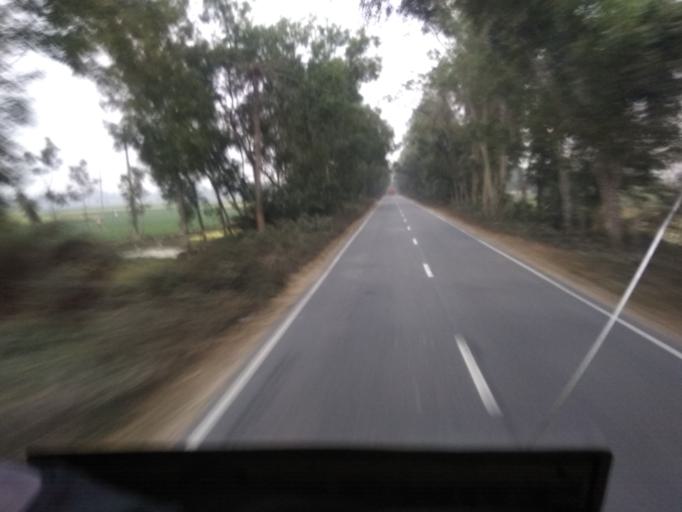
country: BD
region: Rajshahi
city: Bogra
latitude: 24.6968
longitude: 89.3018
